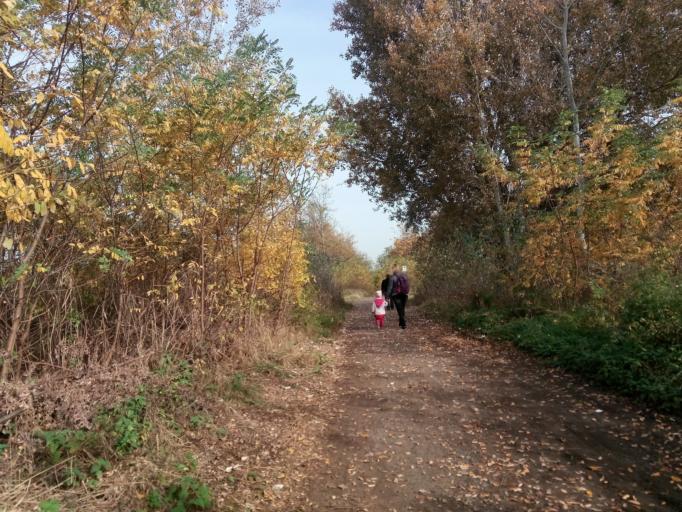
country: HU
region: Pest
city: Vecses
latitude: 47.4201
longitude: 19.2864
